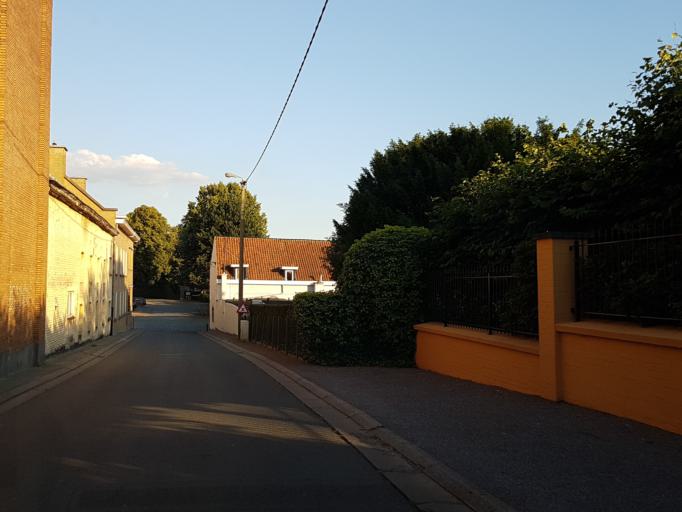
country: BE
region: Flanders
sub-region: Provincie Vlaams-Brabant
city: Merchtem
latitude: 50.9108
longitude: 4.2492
